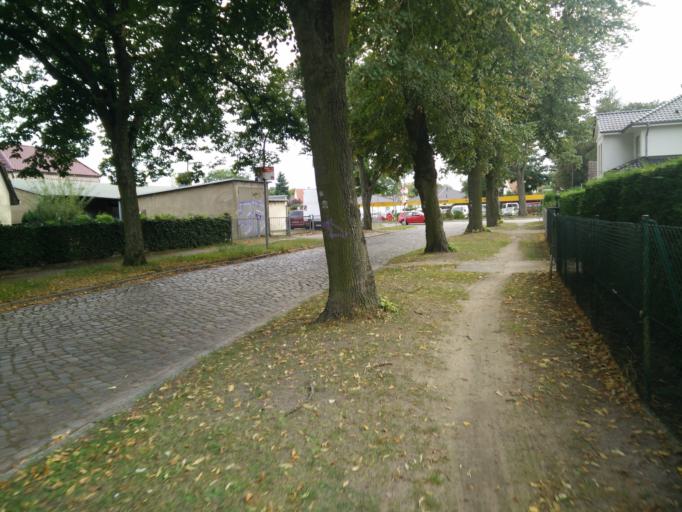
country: DE
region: Brandenburg
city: Falkensee
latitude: 52.5717
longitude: 13.0922
